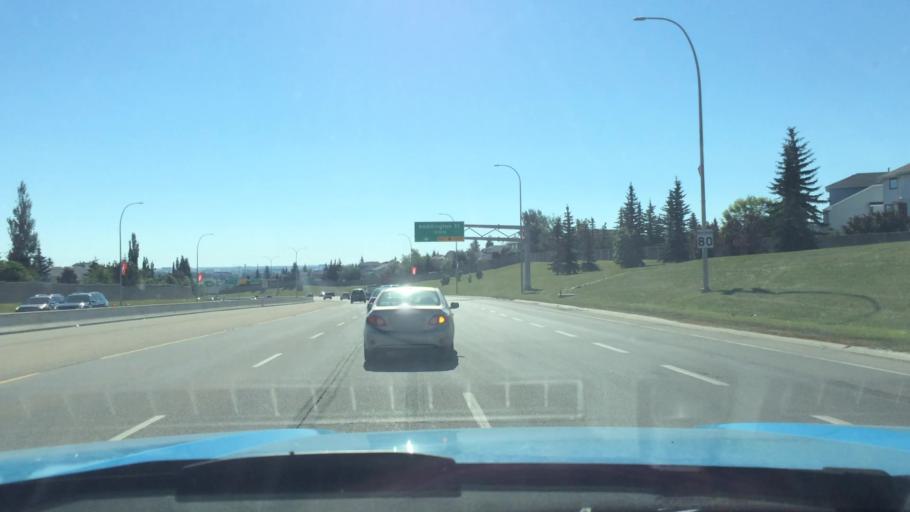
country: CA
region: Alberta
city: Calgary
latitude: 51.1427
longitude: -114.1050
